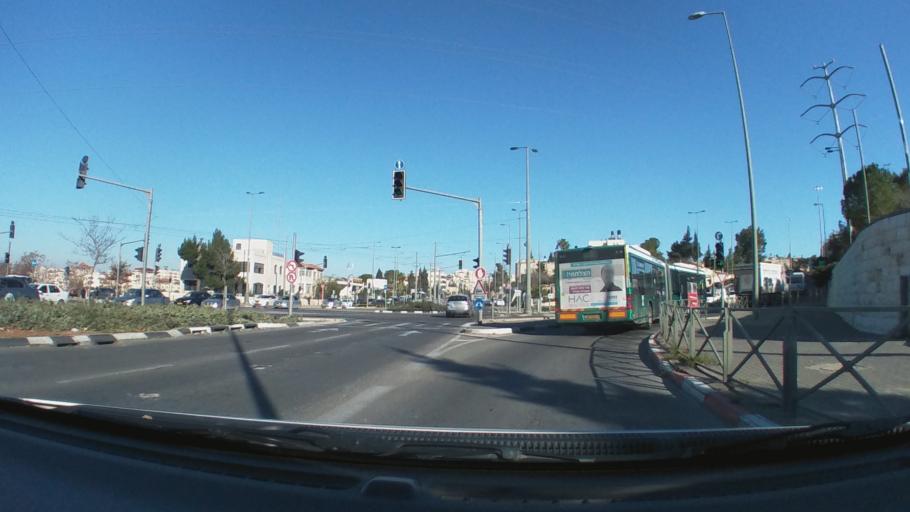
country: PS
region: West Bank
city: East Jerusalem
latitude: 31.8061
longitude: 35.2345
